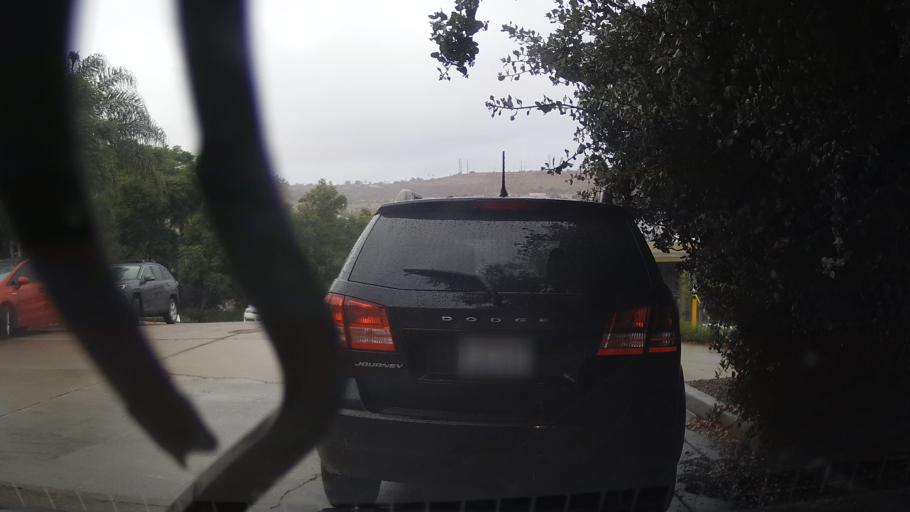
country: US
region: California
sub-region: San Diego County
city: San Diego
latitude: 32.7761
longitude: -117.1197
